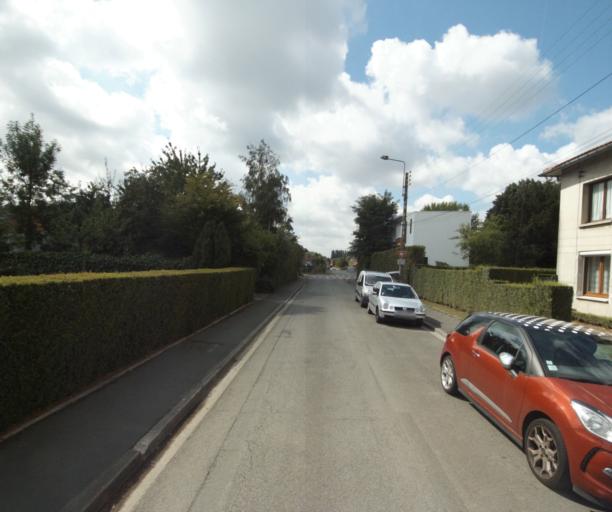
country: FR
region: Nord-Pas-de-Calais
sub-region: Departement du Nord
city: Croix
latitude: 50.6567
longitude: 3.1514
